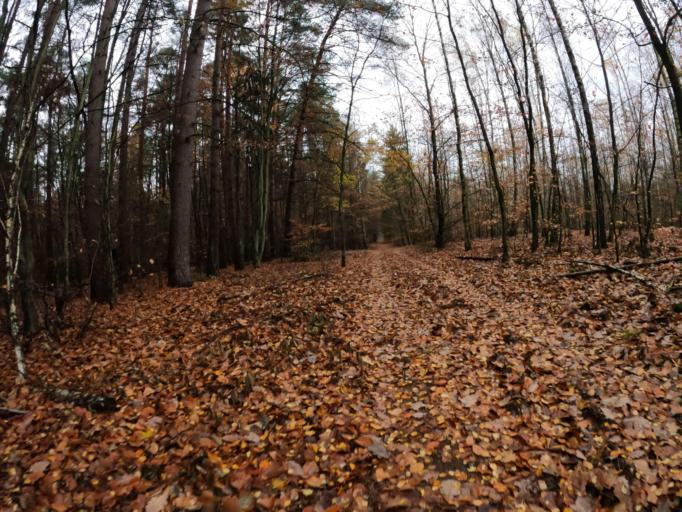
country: PL
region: West Pomeranian Voivodeship
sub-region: Powiat walecki
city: Tuczno
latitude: 53.2634
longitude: 16.2578
